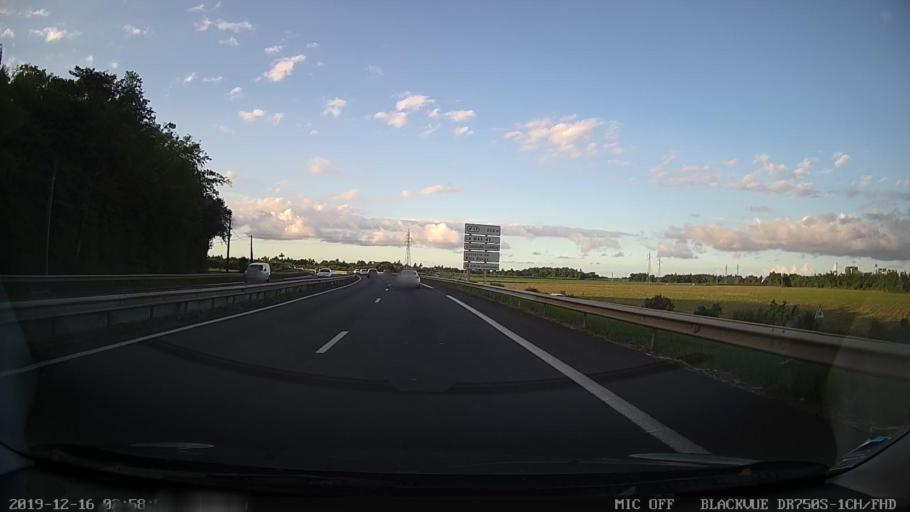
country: RE
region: Reunion
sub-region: Reunion
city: Sainte-Suzanne
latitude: -20.9225
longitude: 55.6267
